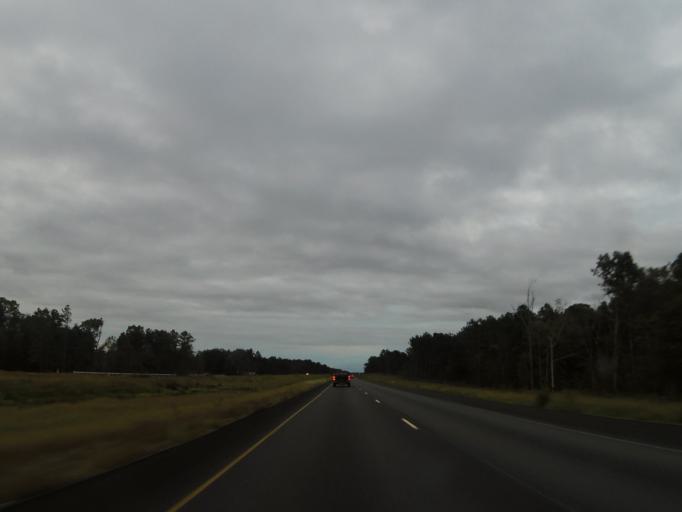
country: US
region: Alabama
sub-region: Etowah County
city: Attalla
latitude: 33.9623
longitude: -86.1295
